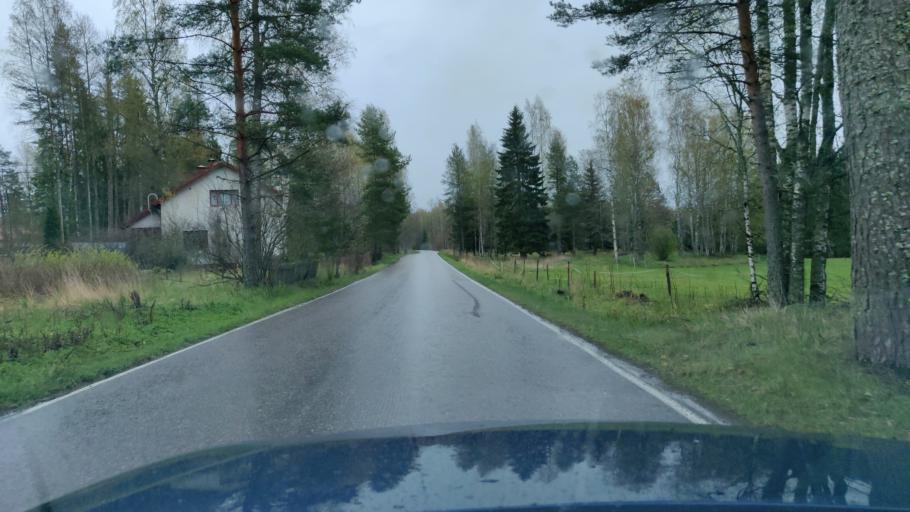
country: FI
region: Uusimaa
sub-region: Helsinki
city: Nurmijaervi
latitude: 60.4996
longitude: 24.6989
